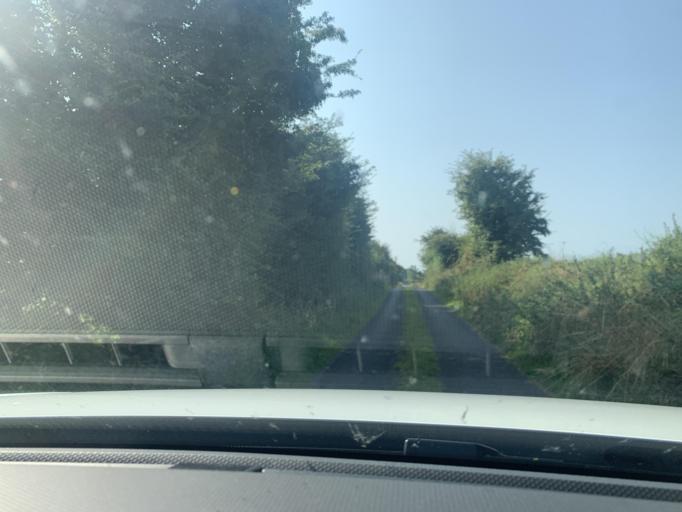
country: IE
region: Connaught
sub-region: Maigh Eo
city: Ballyhaunis
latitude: 53.8069
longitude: -8.7435
